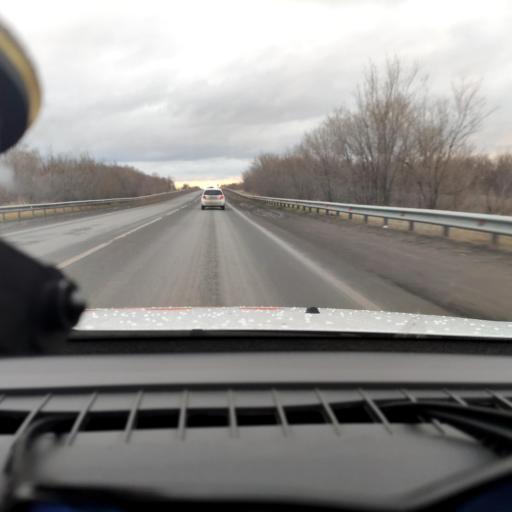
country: RU
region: Samara
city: Samara
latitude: 53.0813
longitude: 50.1035
